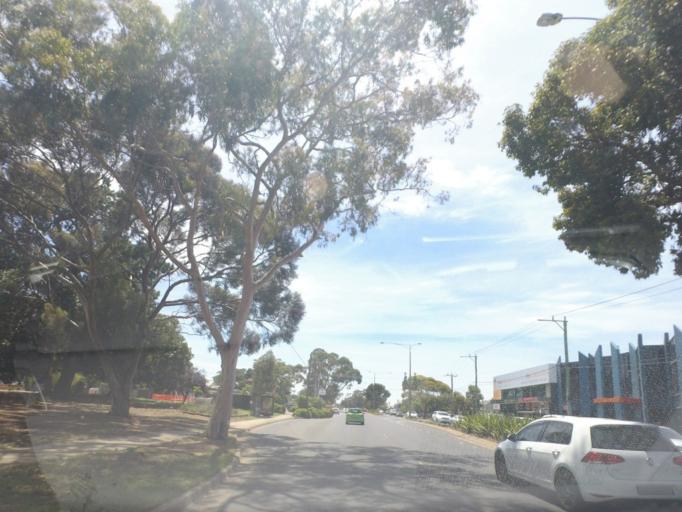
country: AU
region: Victoria
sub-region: Wyndham
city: Werribee
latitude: -37.9014
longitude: 144.6640
